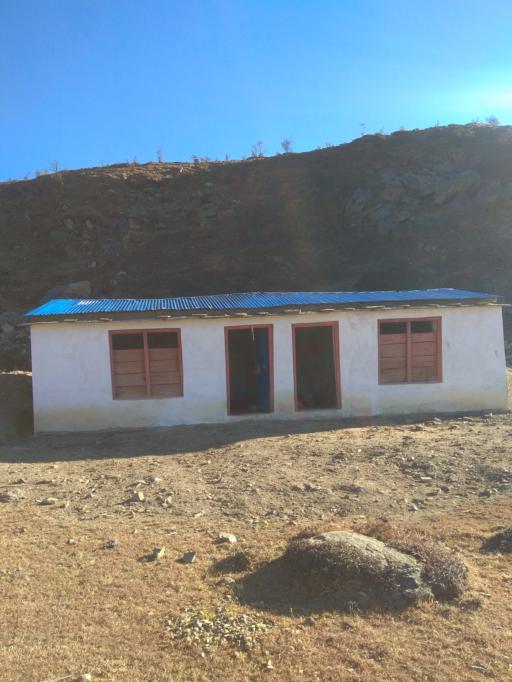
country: NP
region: Far Western
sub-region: Seti Zone
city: Achham
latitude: 29.2785
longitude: 81.6496
